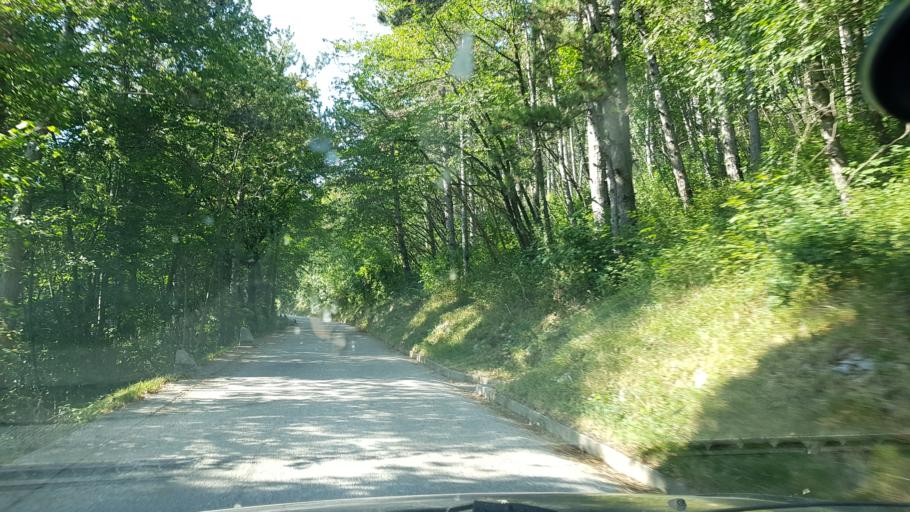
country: SI
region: Nova Gorica
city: Solkan
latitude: 45.9921
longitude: 13.6610
